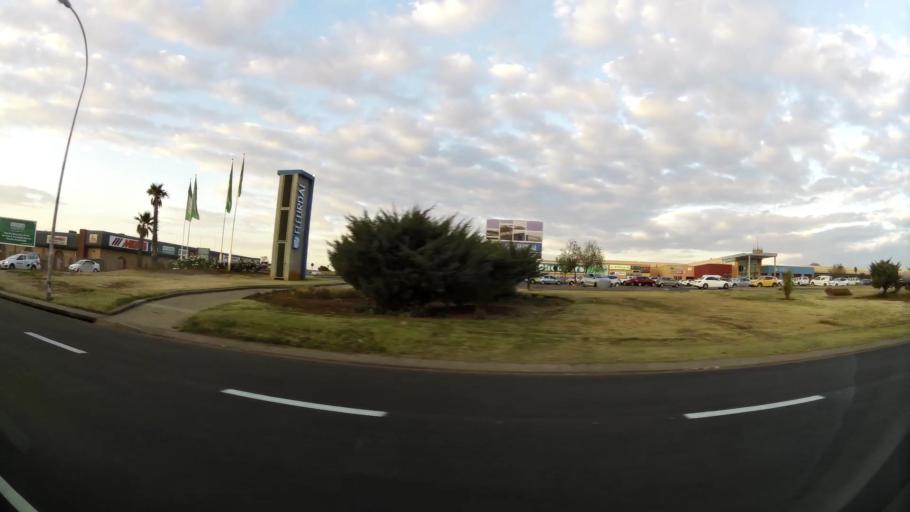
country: ZA
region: Orange Free State
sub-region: Mangaung Metropolitan Municipality
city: Bloemfontein
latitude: -29.1575
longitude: 26.1889
